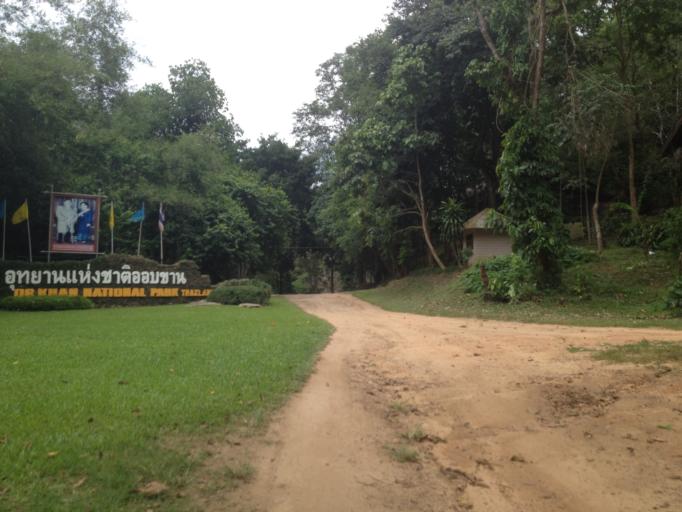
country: TH
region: Chiang Mai
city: Hang Dong
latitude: 18.7192
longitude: 98.8233
